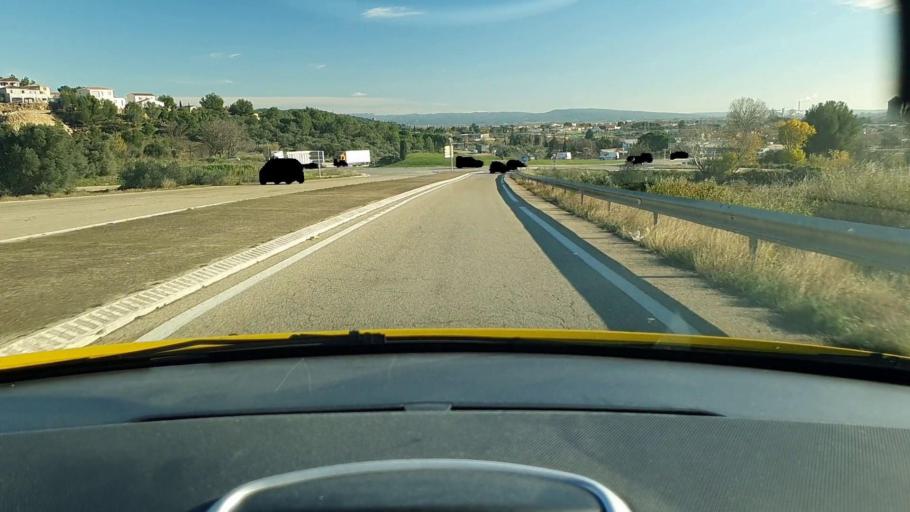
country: FR
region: Languedoc-Roussillon
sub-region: Departement du Gard
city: Comps
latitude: 43.8191
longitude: 4.6104
